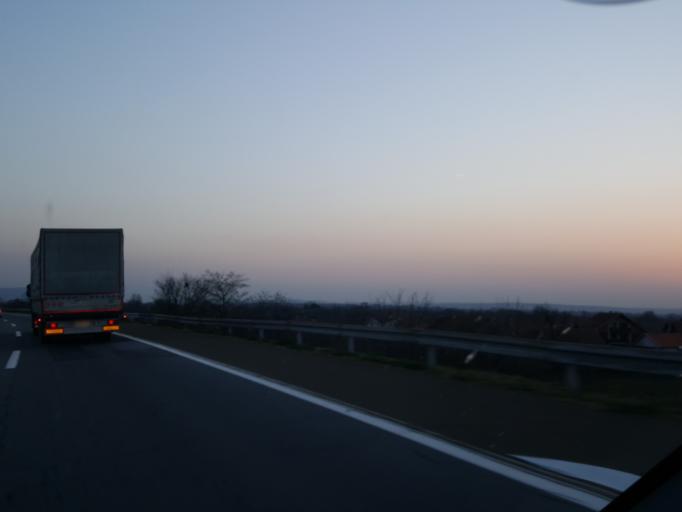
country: RS
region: Central Serbia
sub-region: Rasinski Okrug
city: Cicevac
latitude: 43.7716
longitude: 21.4353
